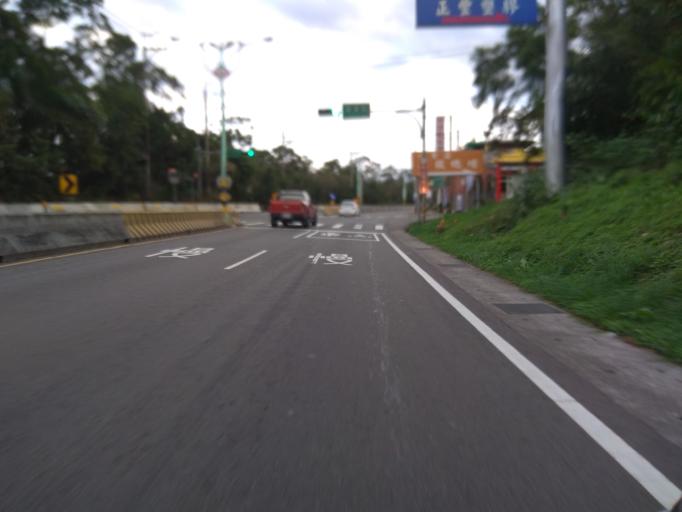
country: TW
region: Taiwan
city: Daxi
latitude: 24.8443
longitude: 121.2107
